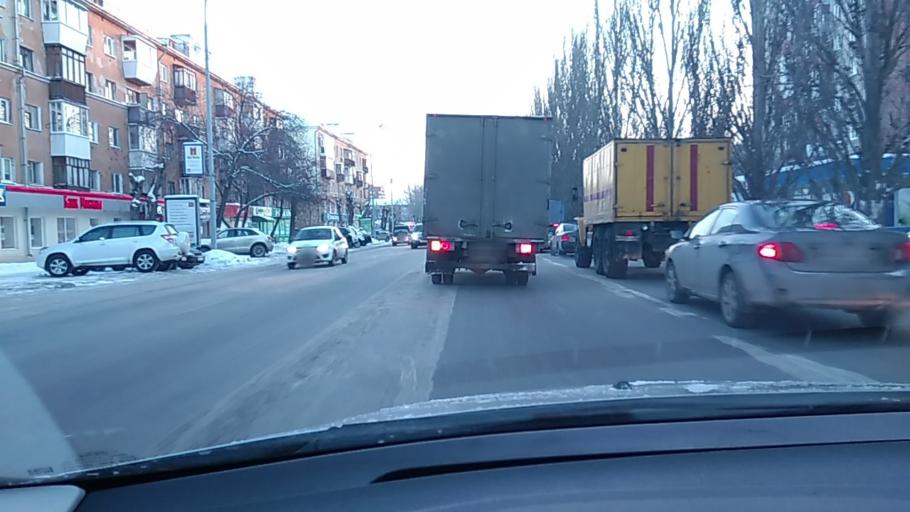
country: RU
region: Sverdlovsk
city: Yekaterinburg
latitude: 56.8322
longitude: 60.6356
